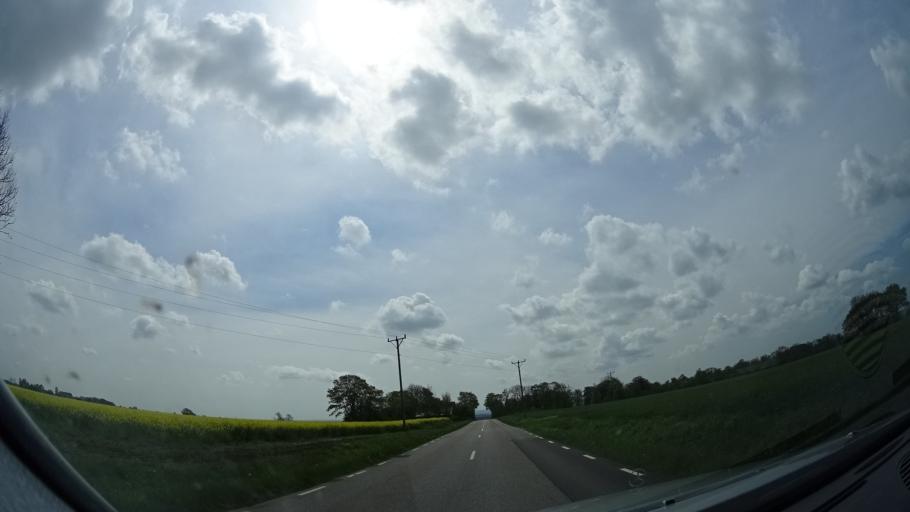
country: SE
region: Skane
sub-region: Hoors Kommun
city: Loberod
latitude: 55.7395
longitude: 13.4947
